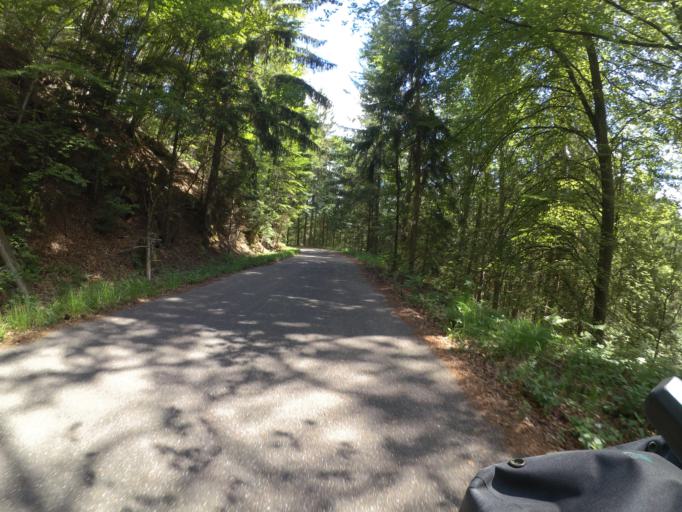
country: DE
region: Rheinland-Pfalz
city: Fischbach
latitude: 49.1338
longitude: 7.7110
